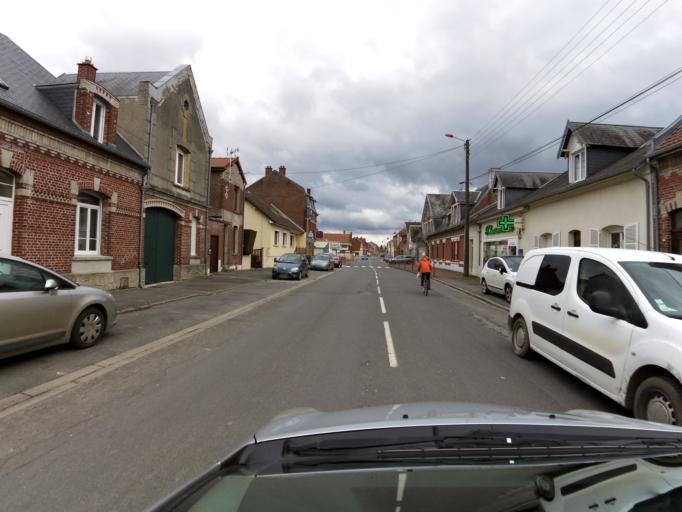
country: FR
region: Picardie
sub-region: Departement de la Somme
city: Chaulnes
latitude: 49.8179
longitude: 2.8033
